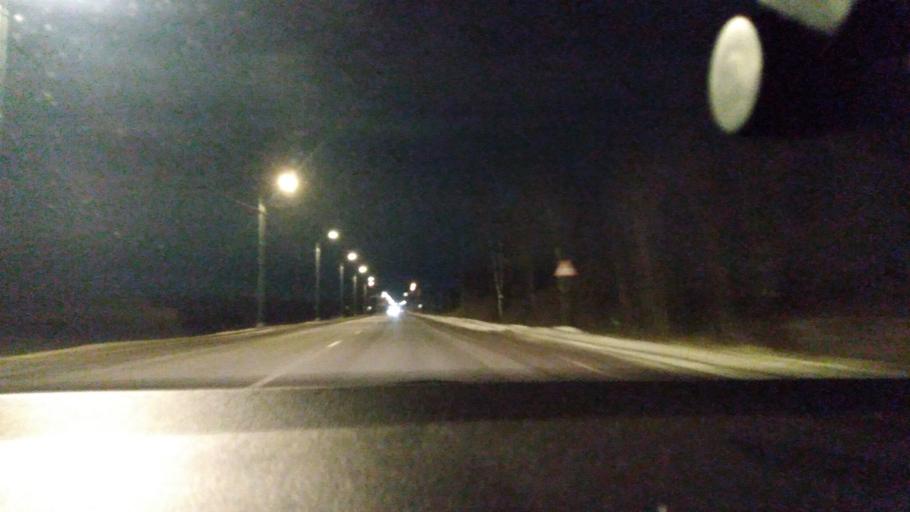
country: RU
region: Moskovskaya
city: Yegor'yevsk
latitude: 55.4110
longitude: 39.0500
